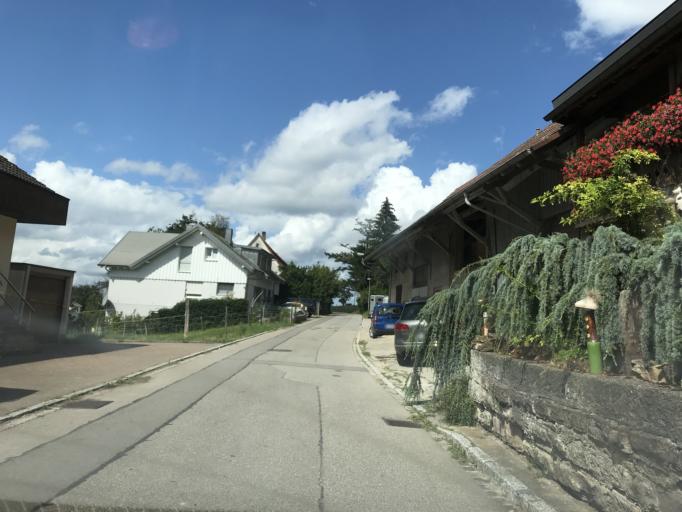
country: DE
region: Baden-Wuerttemberg
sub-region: Freiburg Region
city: Steinen
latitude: 47.6005
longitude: 7.7563
